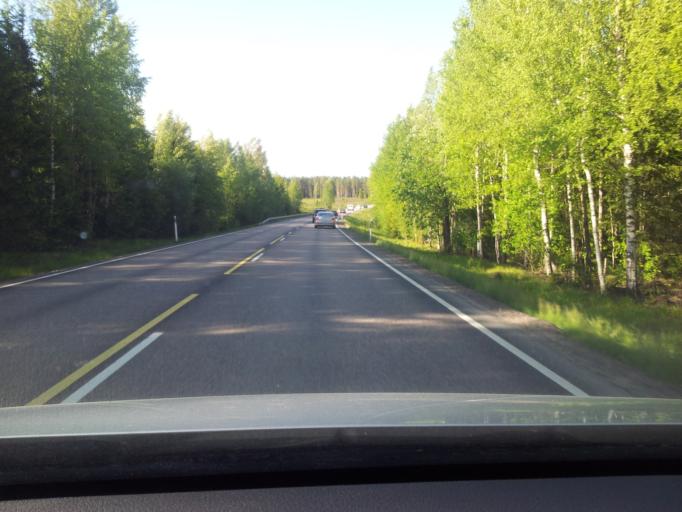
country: FI
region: Kymenlaakso
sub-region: Kouvola
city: Elimaeki
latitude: 60.8485
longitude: 26.5435
